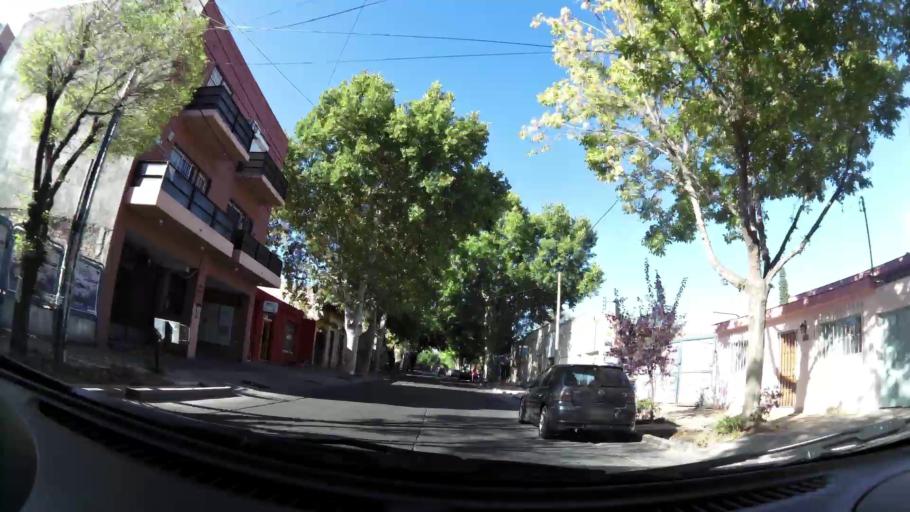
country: AR
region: Mendoza
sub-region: Departamento de Godoy Cruz
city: Godoy Cruz
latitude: -32.9308
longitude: -68.8468
